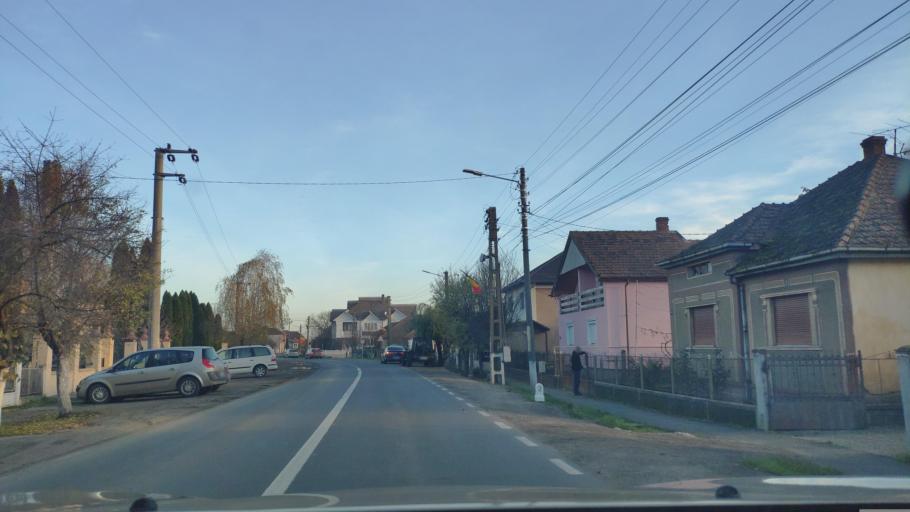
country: RO
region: Satu Mare
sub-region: Comuna Odoreu
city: Odoreu
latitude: 47.7940
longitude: 22.9940
